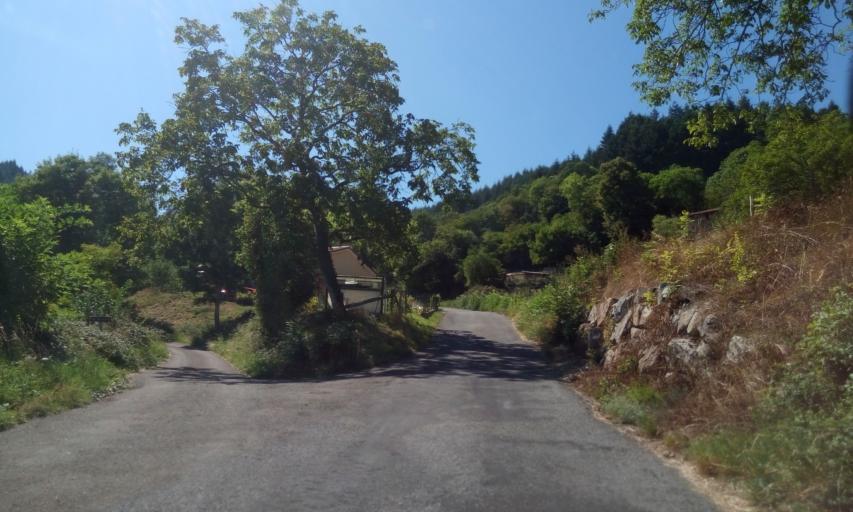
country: FR
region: Rhone-Alpes
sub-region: Departement du Rhone
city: Grandris
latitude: 45.9956
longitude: 4.4371
